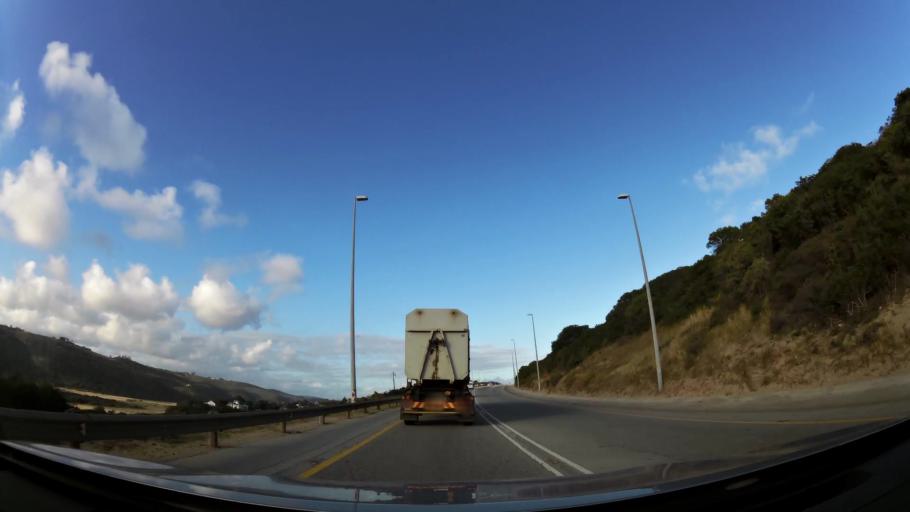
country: ZA
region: Western Cape
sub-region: Eden District Municipality
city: George
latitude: -33.9968
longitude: 22.6068
